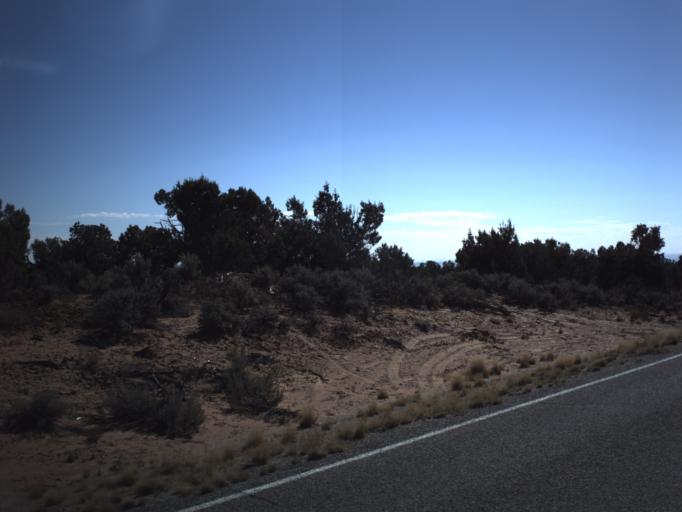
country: US
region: Utah
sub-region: San Juan County
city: Blanding
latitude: 37.2824
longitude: -109.9398
